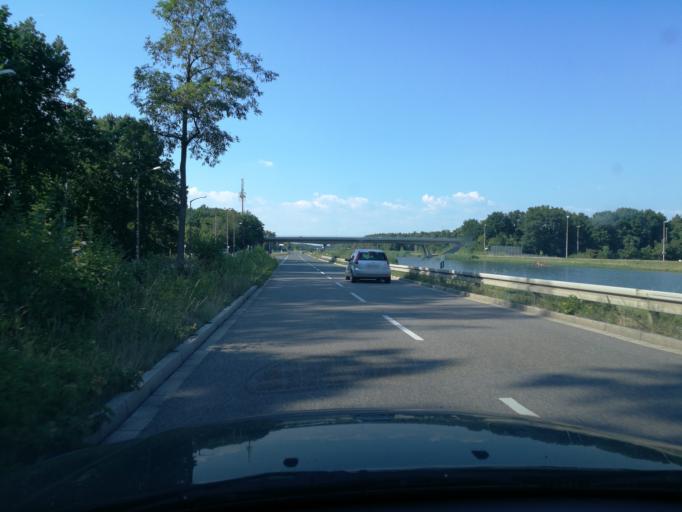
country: DE
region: Bavaria
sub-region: Regierungsbezirk Mittelfranken
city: Erlangen
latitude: 49.5991
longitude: 10.9715
